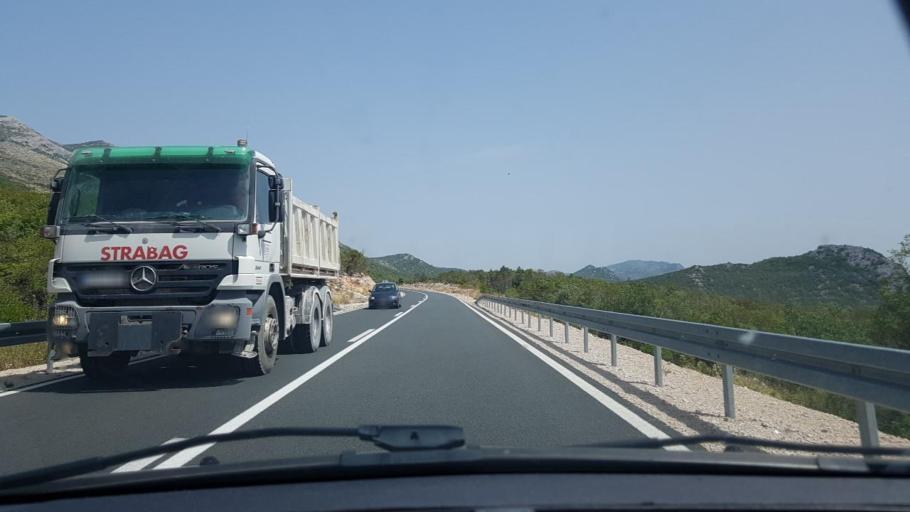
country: BA
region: Federation of Bosnia and Herzegovina
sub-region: Hercegovacko-Bosanski Kanton
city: Neum
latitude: 42.9593
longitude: 17.7123
